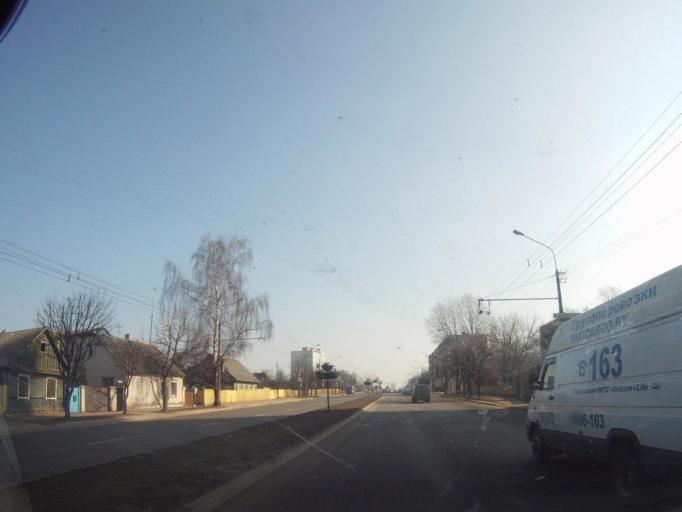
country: BY
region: Minsk
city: Minsk
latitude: 53.9322
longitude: 27.5505
